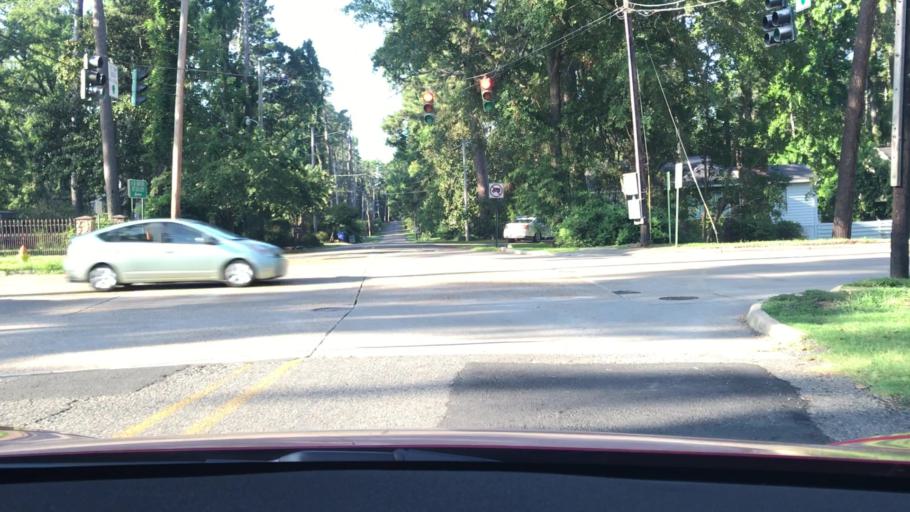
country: US
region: Louisiana
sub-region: Bossier Parish
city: Bossier City
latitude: 32.4549
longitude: -93.7417
